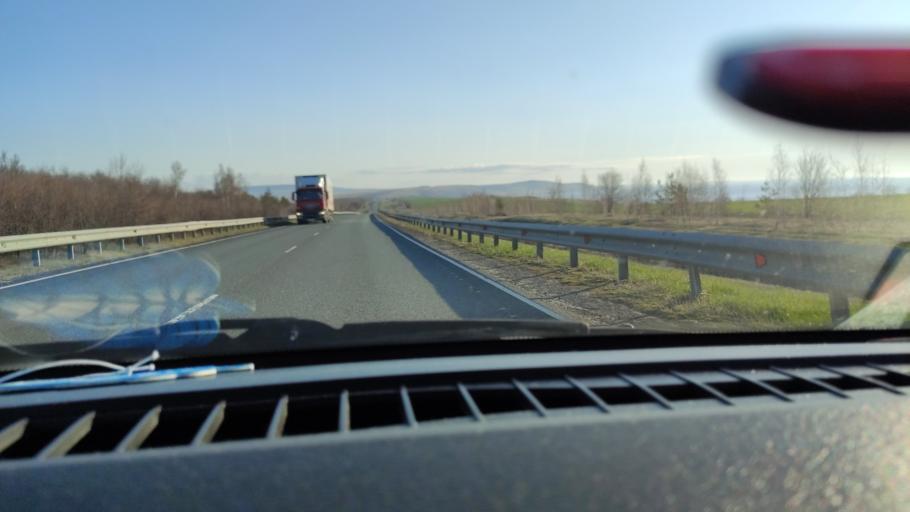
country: RU
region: Saratov
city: Balakovo
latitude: 52.1698
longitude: 47.8292
